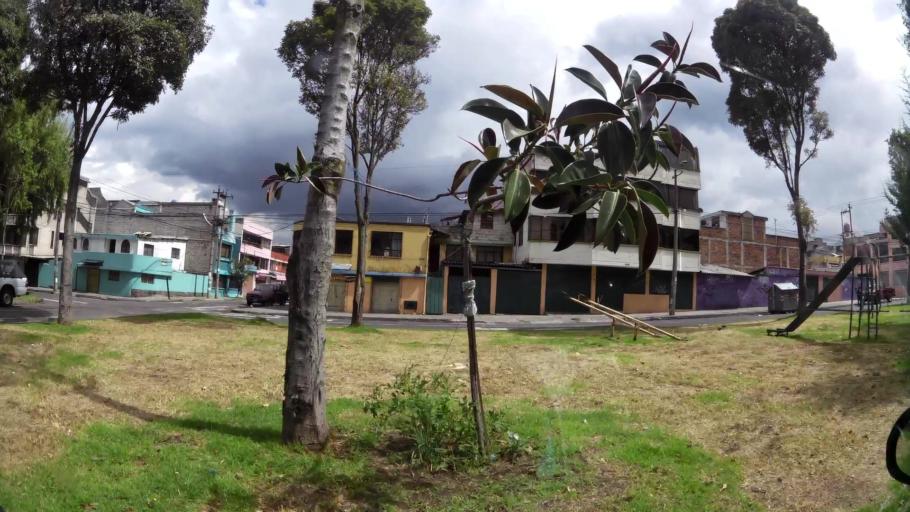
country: EC
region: Pichincha
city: Quito
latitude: -0.2472
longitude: -78.5325
